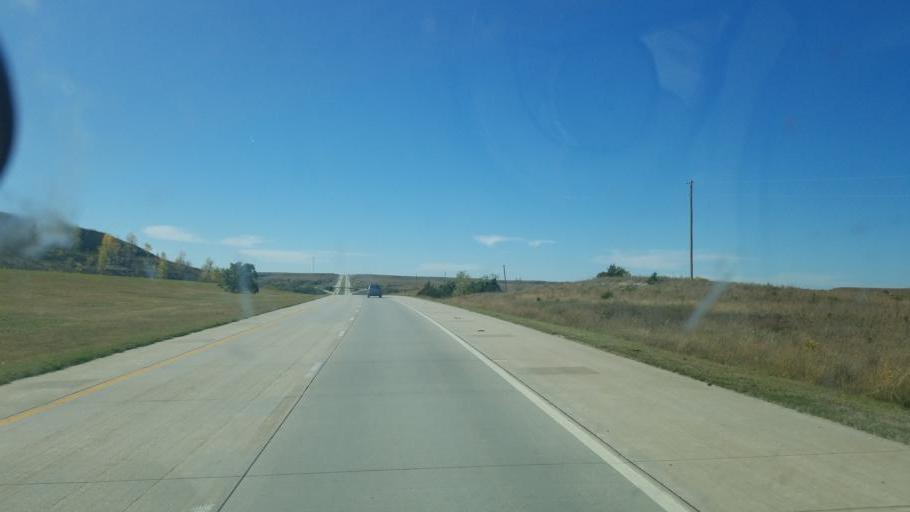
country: US
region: Kansas
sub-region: Riley County
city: Ogden
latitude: 39.0677
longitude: -96.6346
